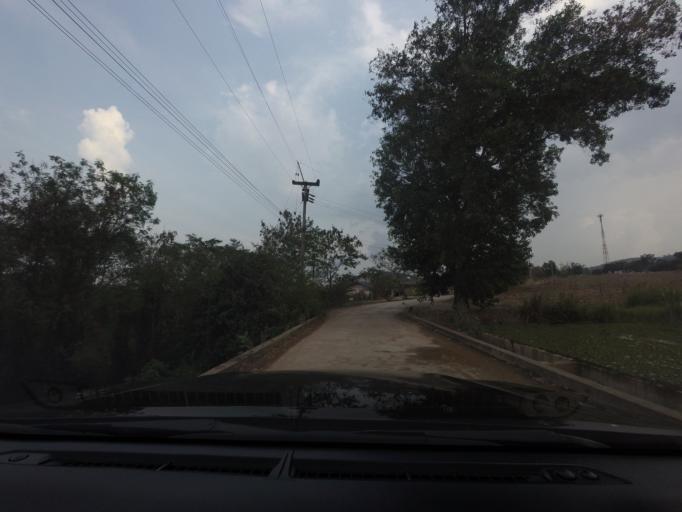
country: TH
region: Nakhon Ratchasima
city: Wang Nam Khiao
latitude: 14.3981
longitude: 101.7940
